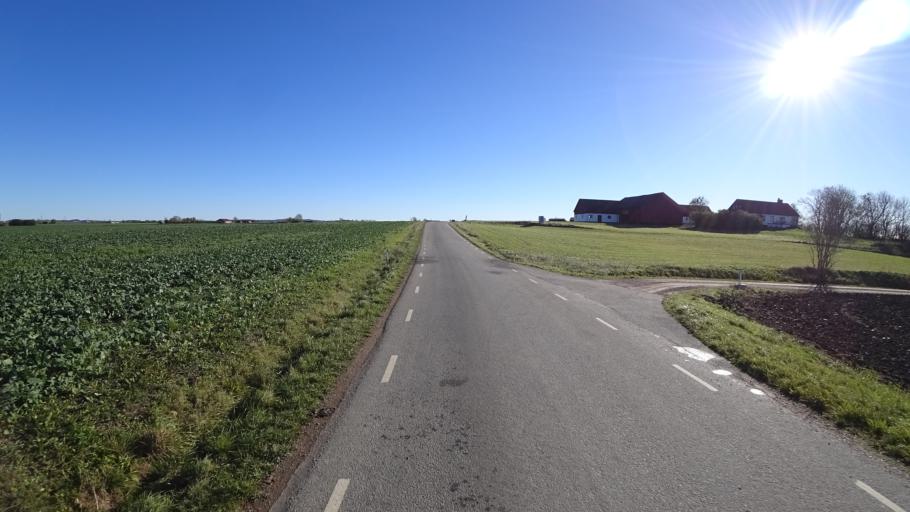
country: SE
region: Skane
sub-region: Svedala Kommun
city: Klagerup
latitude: 55.6162
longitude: 13.2829
